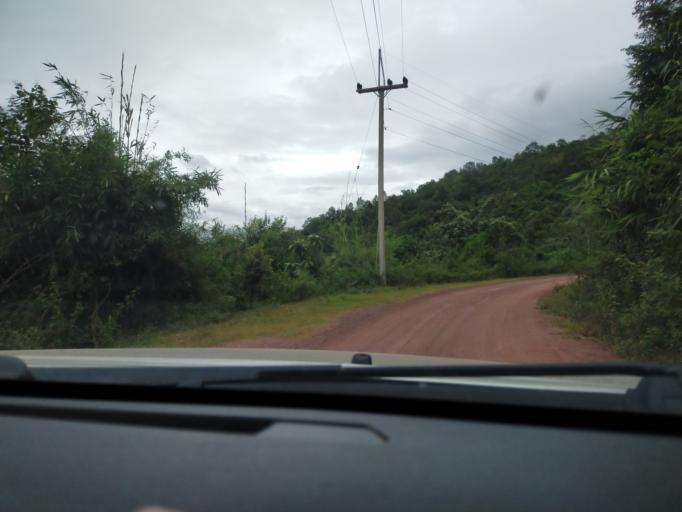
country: TH
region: Nan
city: Chaloem Phra Kiat
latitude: 19.7680
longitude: 101.3487
